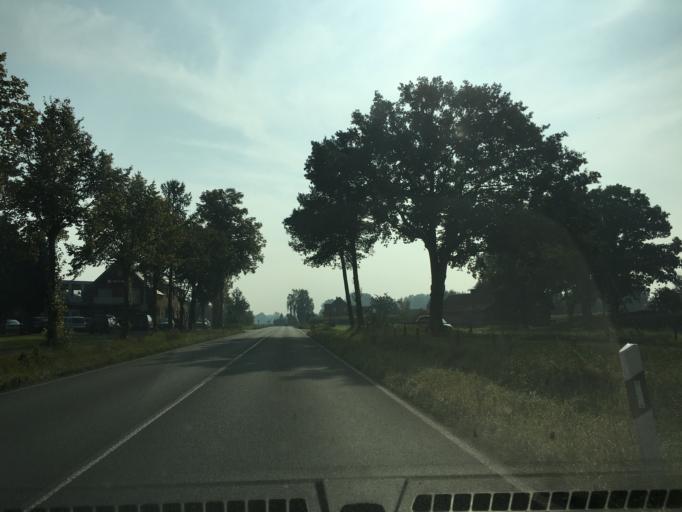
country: DE
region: North Rhine-Westphalia
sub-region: Regierungsbezirk Munster
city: Dulmen
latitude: 51.7894
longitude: 7.3451
